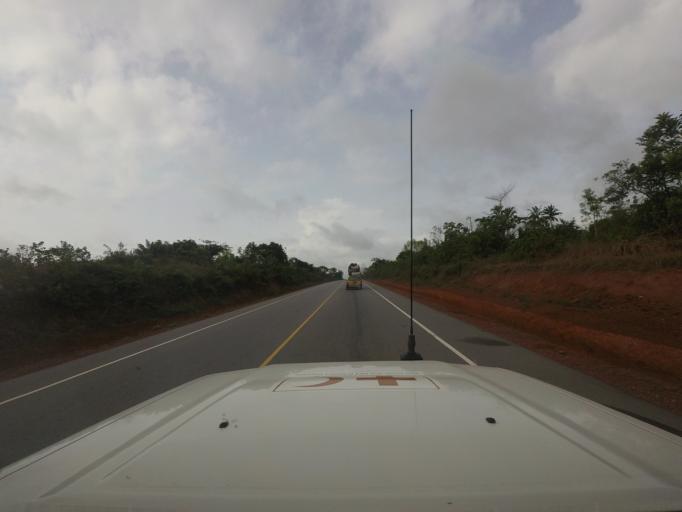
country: LR
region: Bong
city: Gbarnga
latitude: 7.0323
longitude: -9.2695
